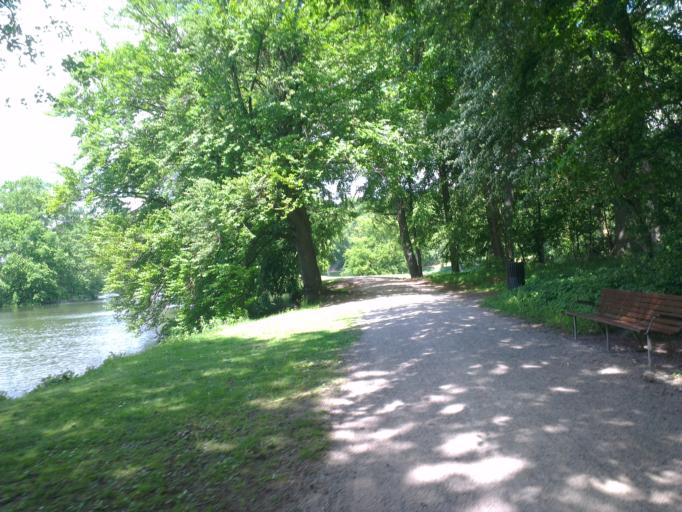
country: DK
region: Capital Region
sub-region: Hillerod Kommune
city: Hillerod
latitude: 55.9394
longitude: 12.3010
